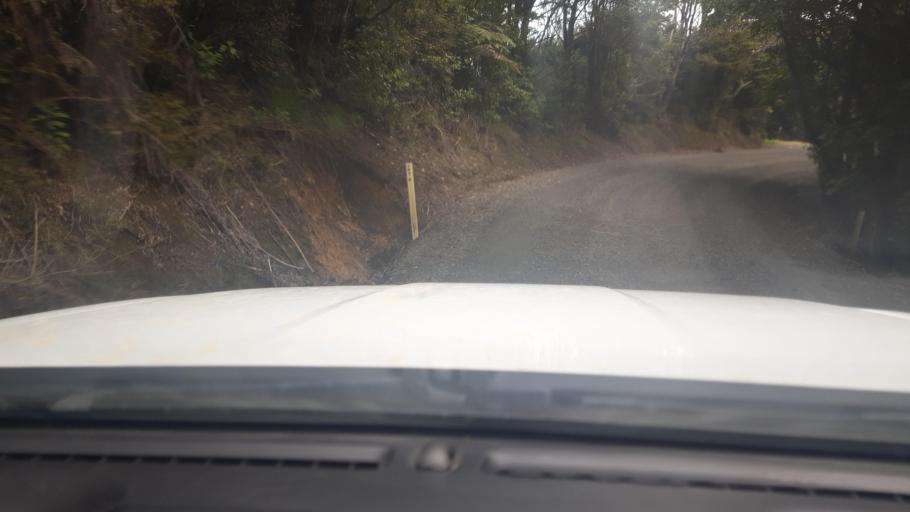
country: NZ
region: Northland
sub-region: Far North District
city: Kaitaia
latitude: -35.0665
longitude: 173.3295
